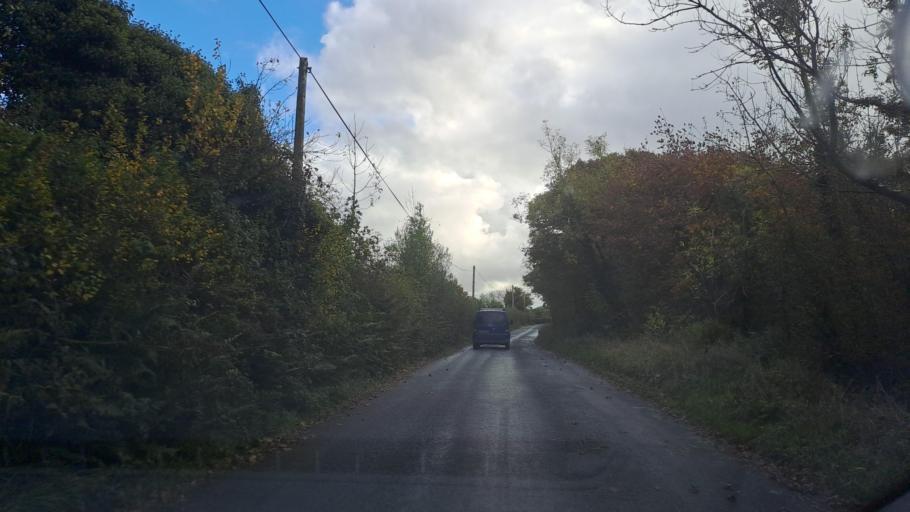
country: IE
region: Ulster
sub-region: An Cabhan
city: Bailieborough
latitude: 53.9961
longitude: -6.9498
